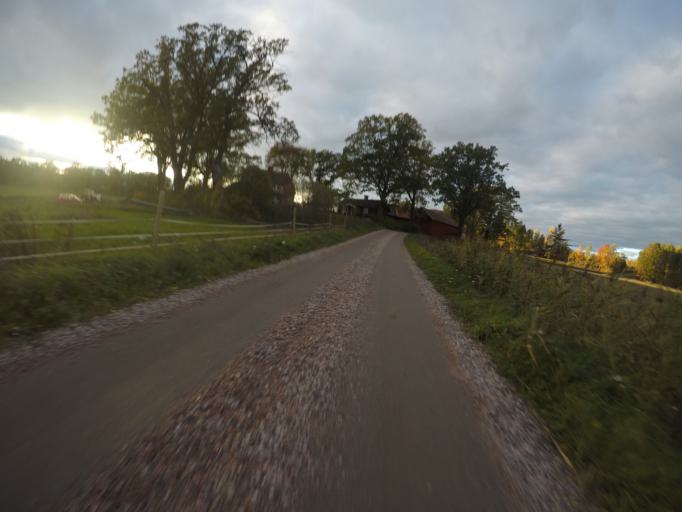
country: SE
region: Vaestmanland
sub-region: Arboga Kommun
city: Tyringe
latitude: 59.3010
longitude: 16.0046
